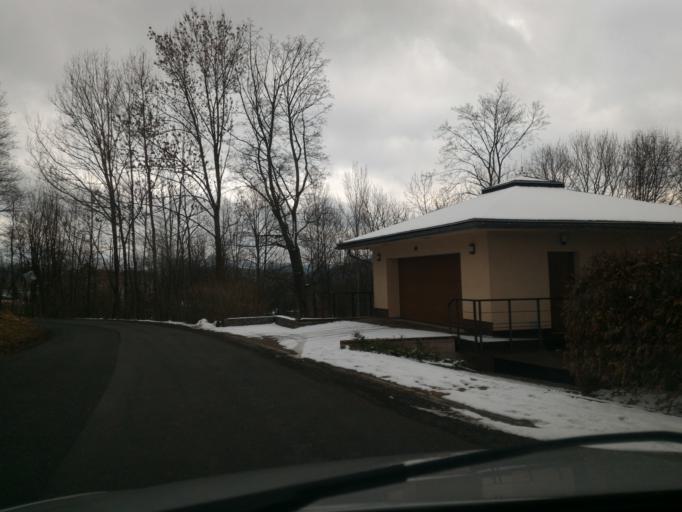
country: CZ
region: Liberecky
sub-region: Okres Jablonec nad Nisou
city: Smrzovka
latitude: 50.7319
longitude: 15.2416
